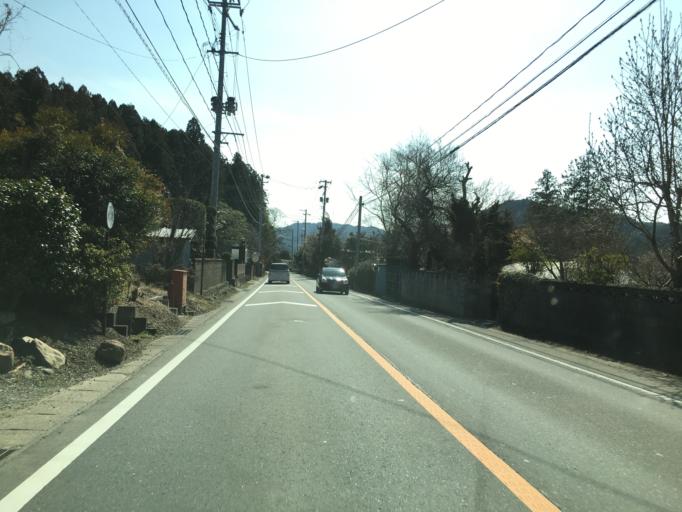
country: JP
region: Ibaraki
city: Daigo
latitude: 36.8836
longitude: 140.4200
